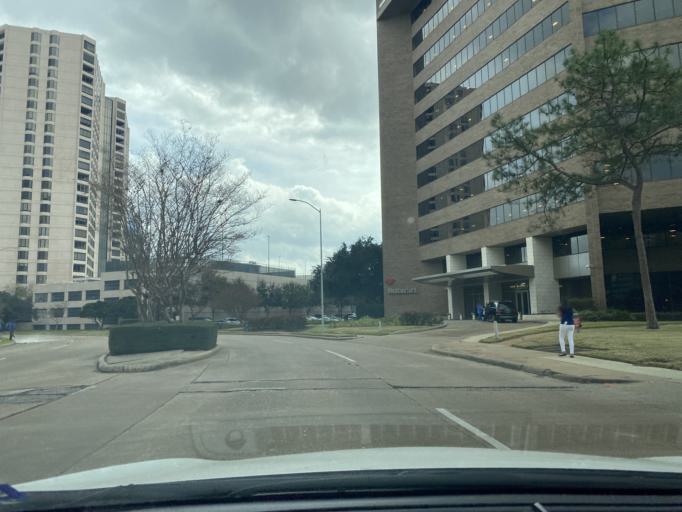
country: US
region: Texas
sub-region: Harris County
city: Hunters Creek Village
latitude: 29.7464
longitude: -95.4730
